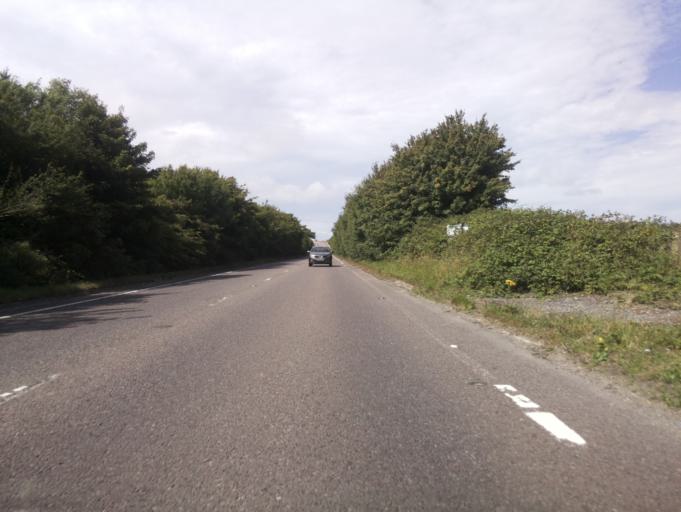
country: GB
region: England
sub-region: Dorset
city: Dorchester
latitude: 50.7742
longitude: -2.5391
